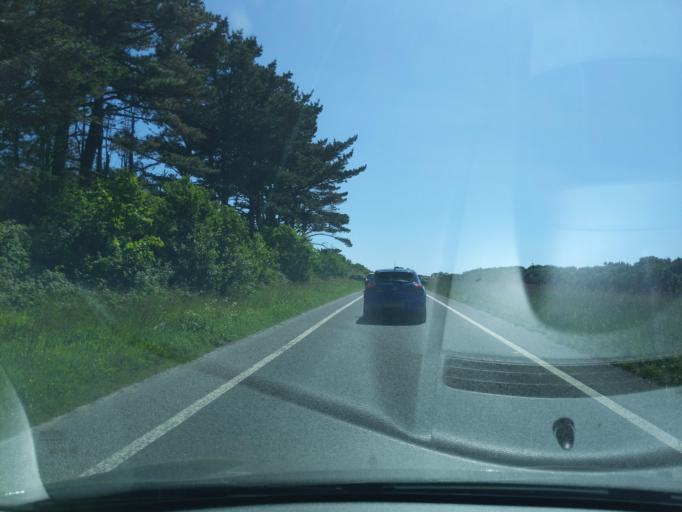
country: GB
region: England
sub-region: Cornwall
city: Penryn
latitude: 50.1683
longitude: -5.1485
